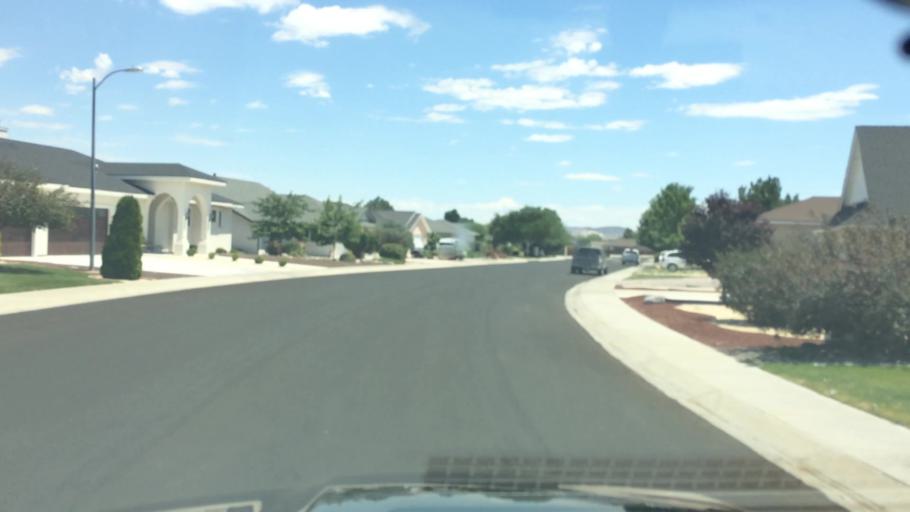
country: US
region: Nevada
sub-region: Lyon County
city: Fernley
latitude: 39.5843
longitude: -119.1461
